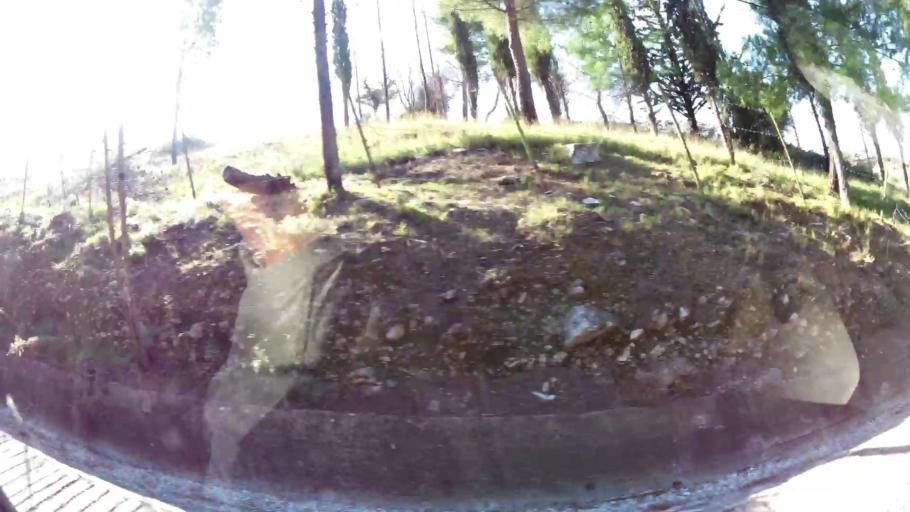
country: GR
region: Attica
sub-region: Nomarchia Athinas
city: Ilioupoli
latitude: 37.9430
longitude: 23.7755
